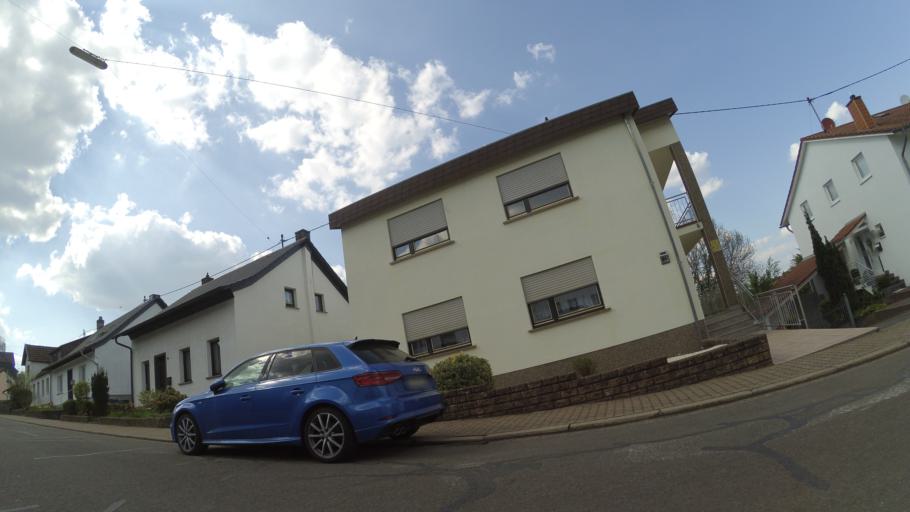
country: DE
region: Saarland
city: Riegelsberg
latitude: 49.3020
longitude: 6.9366
